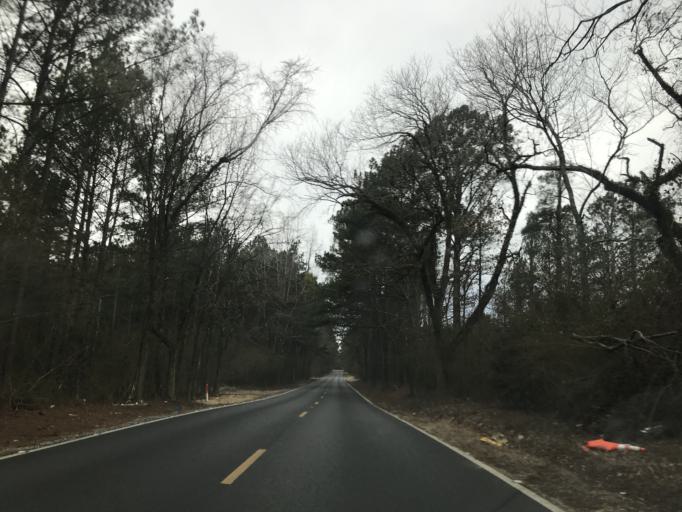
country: US
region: Alabama
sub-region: Shelby County
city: Shoal Creek
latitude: 33.4707
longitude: -86.6336
